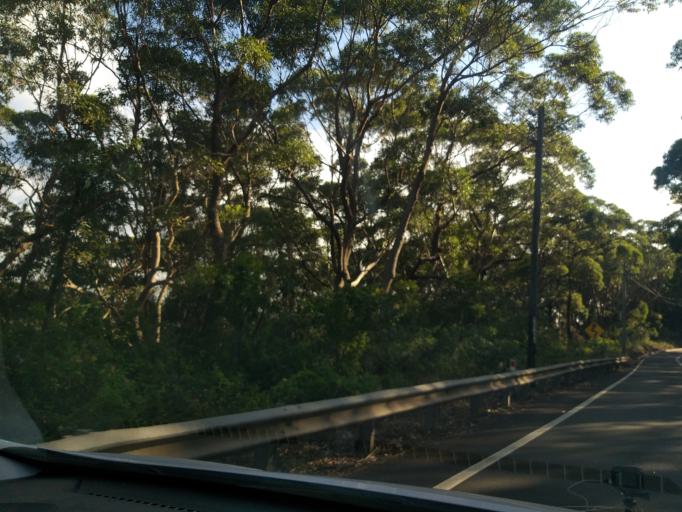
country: AU
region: New South Wales
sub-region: Wollongong
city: Helensburgh
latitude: -34.2212
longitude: 150.9864
